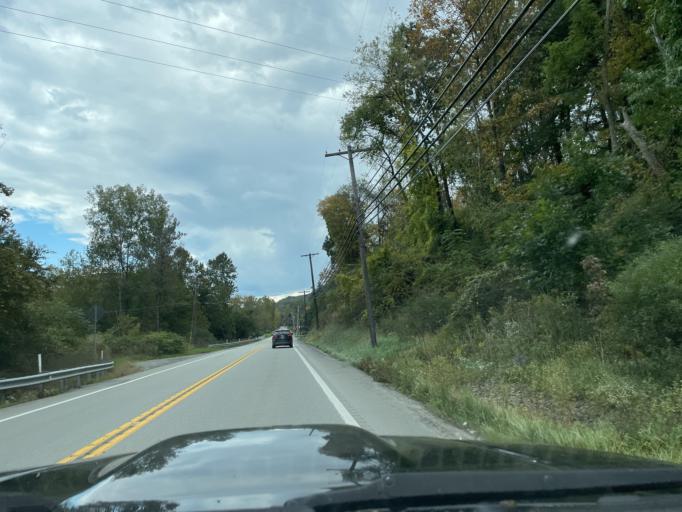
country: US
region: Pennsylvania
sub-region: Westmoreland County
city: Lower Burrell
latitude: 40.5397
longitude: -79.7215
